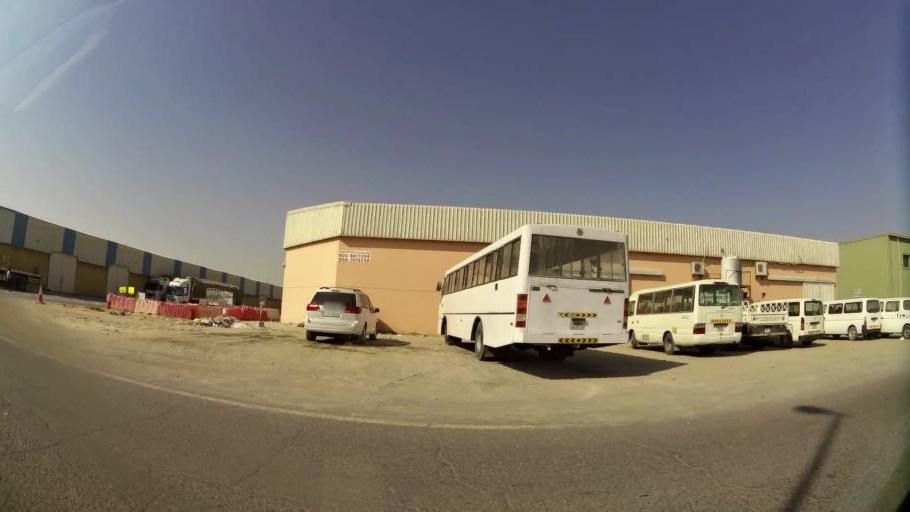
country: AE
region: Ajman
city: Ajman
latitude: 25.4390
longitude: 55.5247
